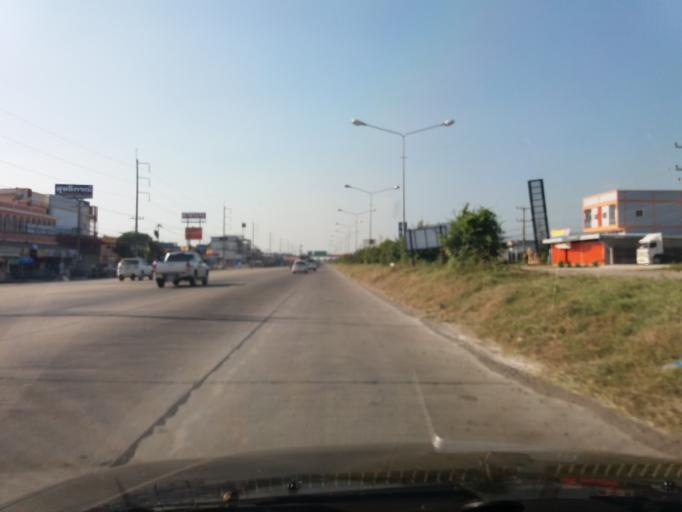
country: TH
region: Nakhon Sawan
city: Kao Liao
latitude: 15.7606
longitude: 99.9944
